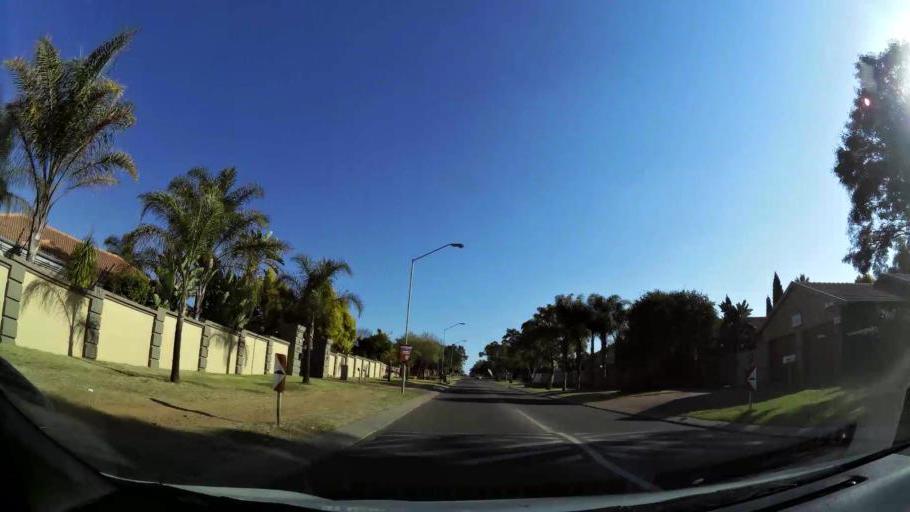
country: ZA
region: Gauteng
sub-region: City of Tshwane Metropolitan Municipality
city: Centurion
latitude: -25.8352
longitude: 28.2977
